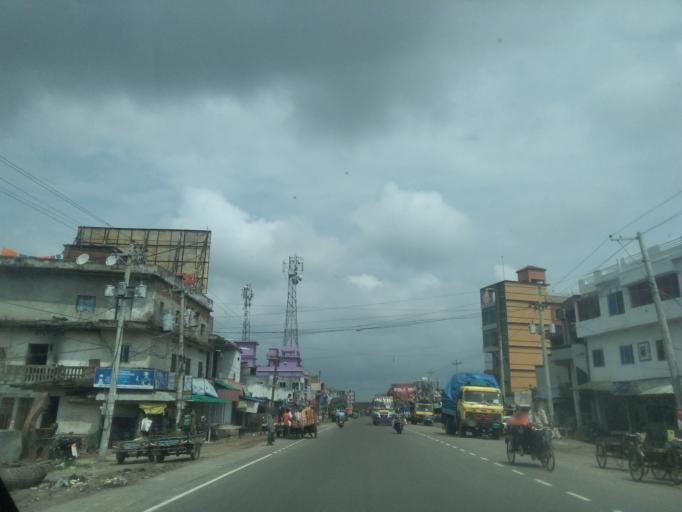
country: BD
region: Khulna
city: Kesabpur
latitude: 22.8397
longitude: 89.2976
